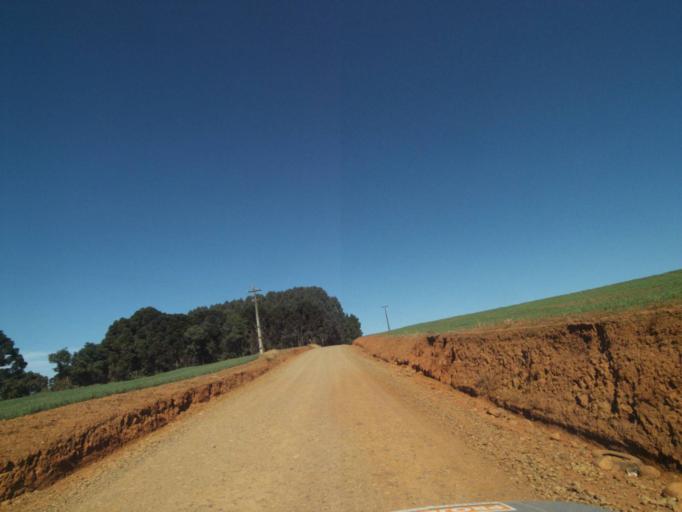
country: BR
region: Parana
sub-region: Tibagi
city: Tibagi
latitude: -24.6105
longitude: -50.6057
